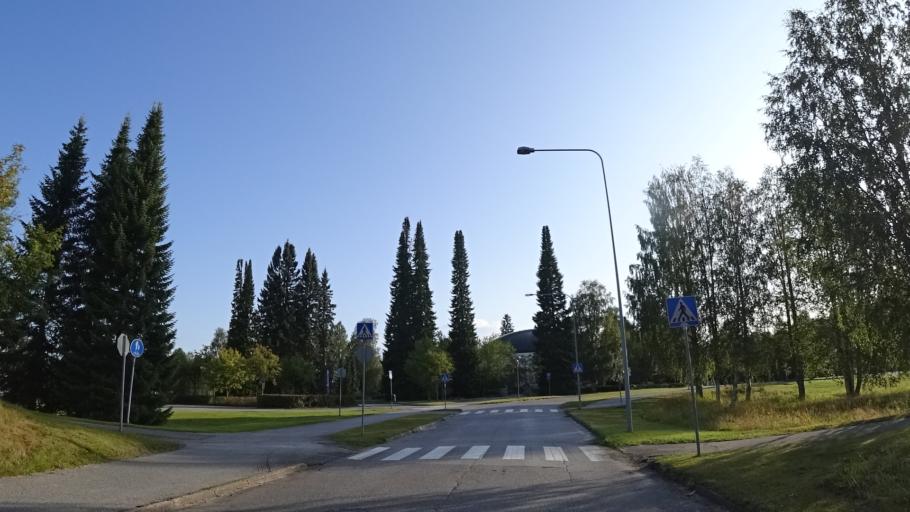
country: FI
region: North Karelia
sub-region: Pielisen Karjala
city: Lieksa
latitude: 63.3141
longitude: 30.0319
